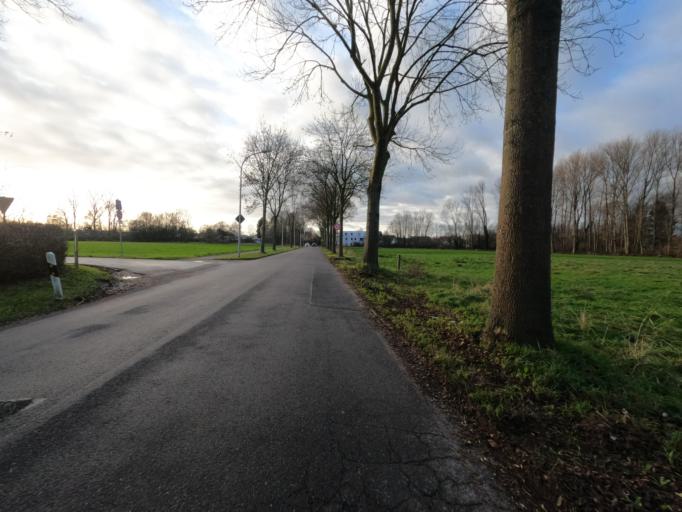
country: DE
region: North Rhine-Westphalia
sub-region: Regierungsbezirk Koln
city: Heinsberg
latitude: 51.0786
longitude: 6.0812
